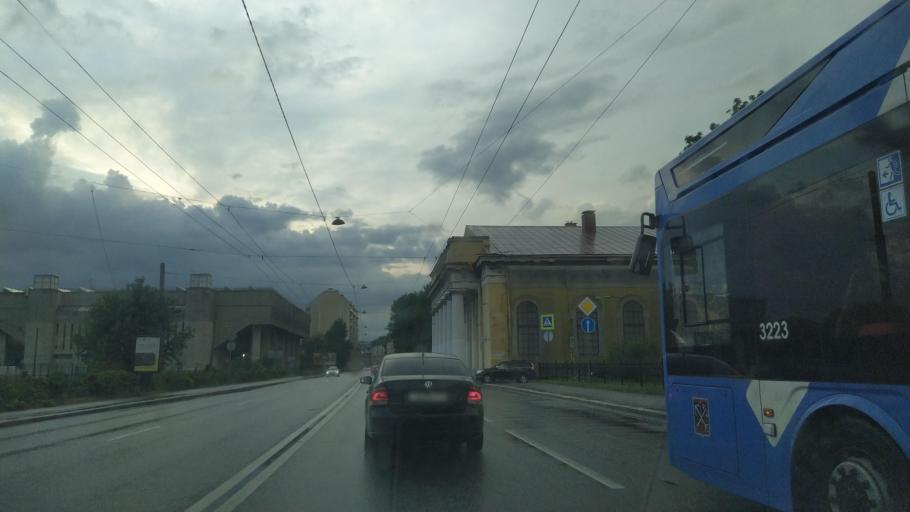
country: RU
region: Leningrad
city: Krestovskiy ostrov
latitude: 59.9567
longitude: 30.2827
